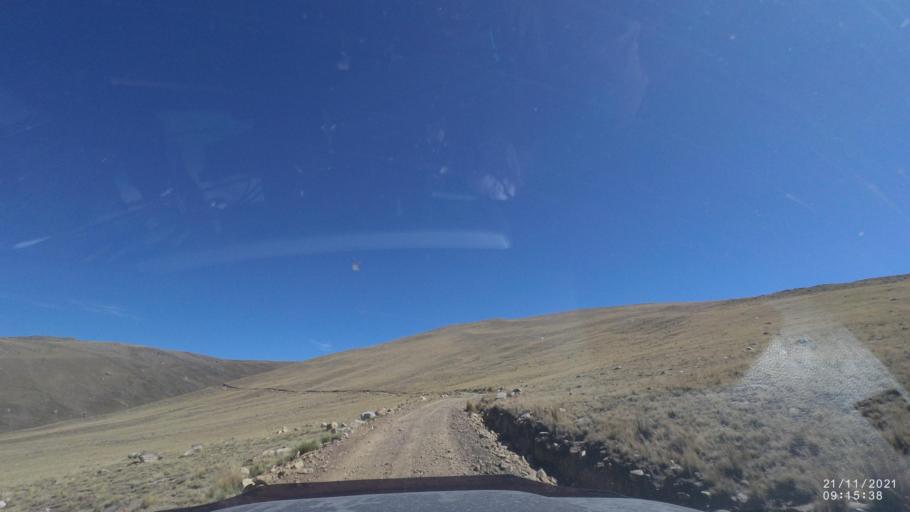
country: BO
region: Cochabamba
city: Cochabamba
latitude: -17.1294
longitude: -66.2575
